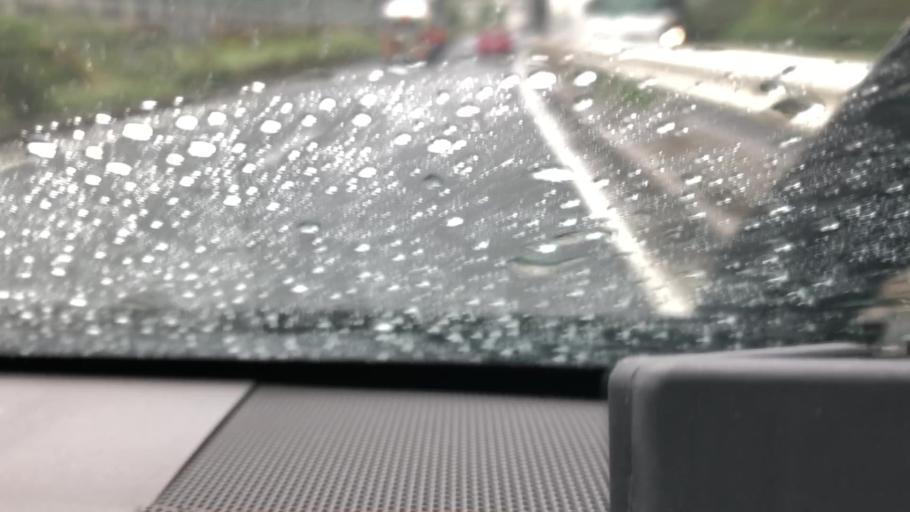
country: JP
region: Kanagawa
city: Yokohama
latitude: 35.4420
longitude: 139.5924
